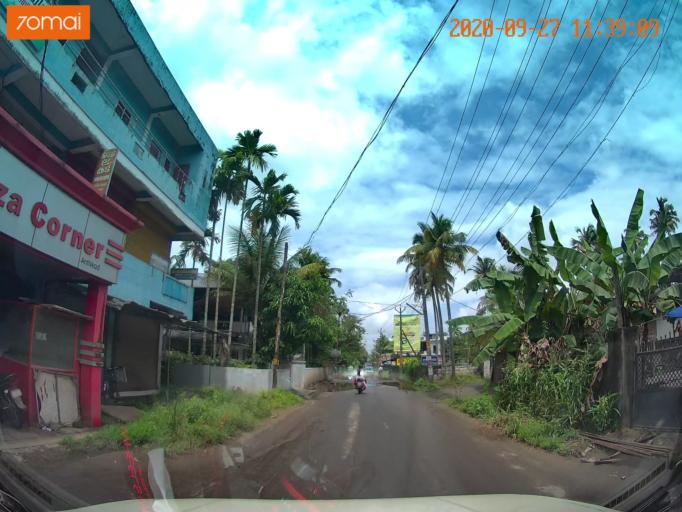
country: IN
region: Kerala
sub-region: Thrissur District
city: Thanniyam
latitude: 10.4635
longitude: 76.1189
